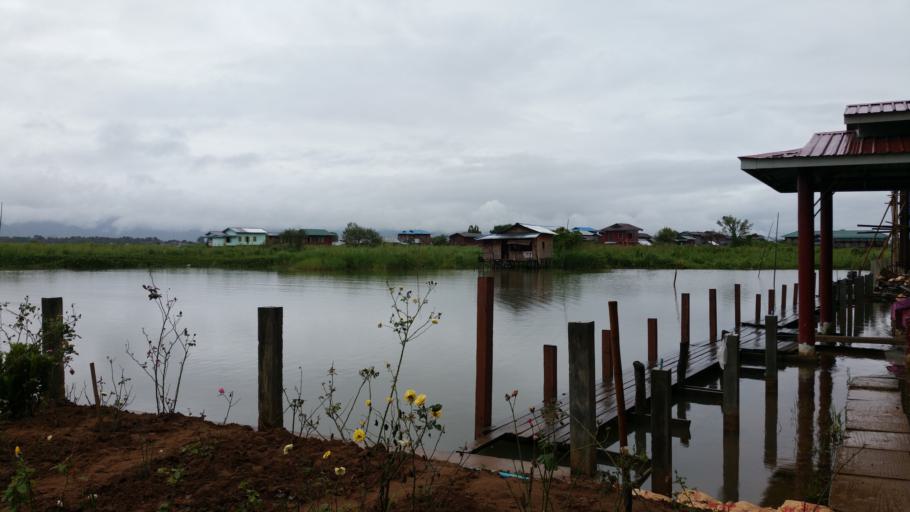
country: MM
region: Shan
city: Taunggyi
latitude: 20.4999
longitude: 96.8965
